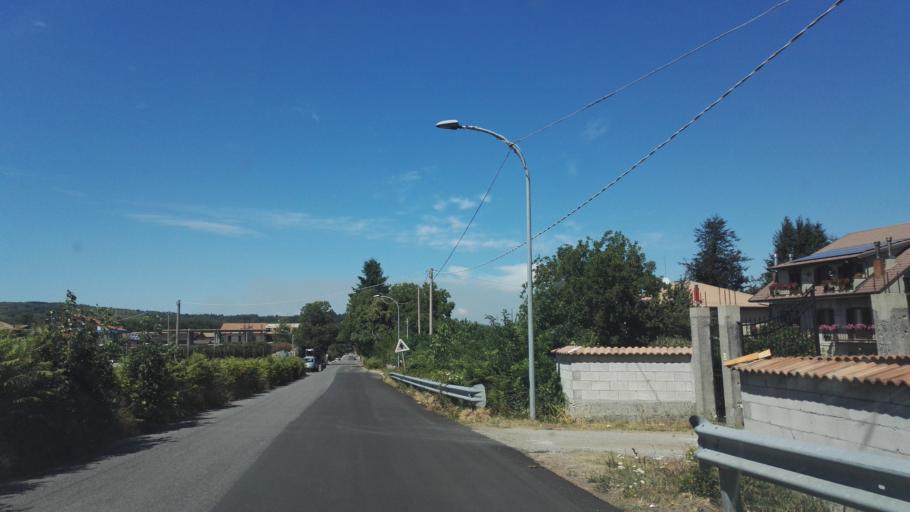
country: IT
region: Calabria
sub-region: Provincia di Vibo-Valentia
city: Serra San Bruno
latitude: 38.5631
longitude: 16.3260
